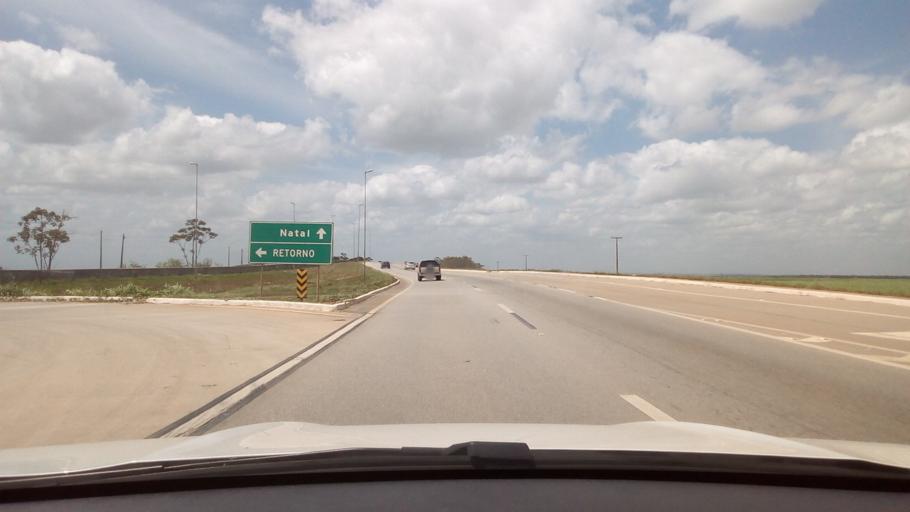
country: BR
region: Paraiba
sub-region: Mamanguape
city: Mamanguape
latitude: -6.9296
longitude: -35.1040
